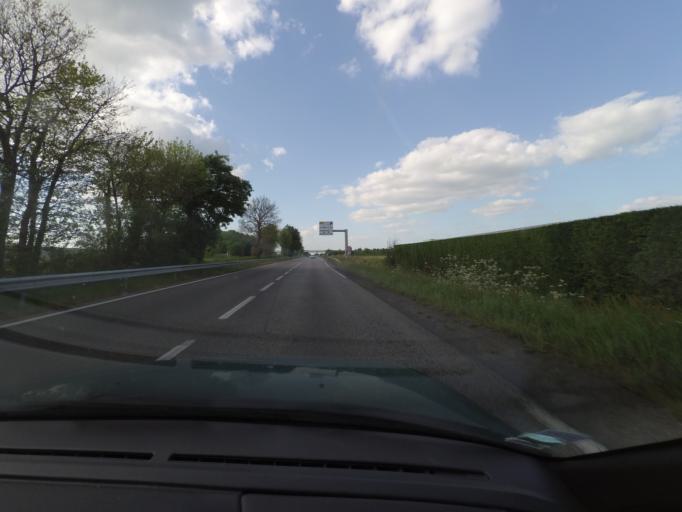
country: FR
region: Pays de la Loire
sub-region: Departement de la Vendee
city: Mouilleron-le-Captif
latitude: 46.7420
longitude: -1.4302
